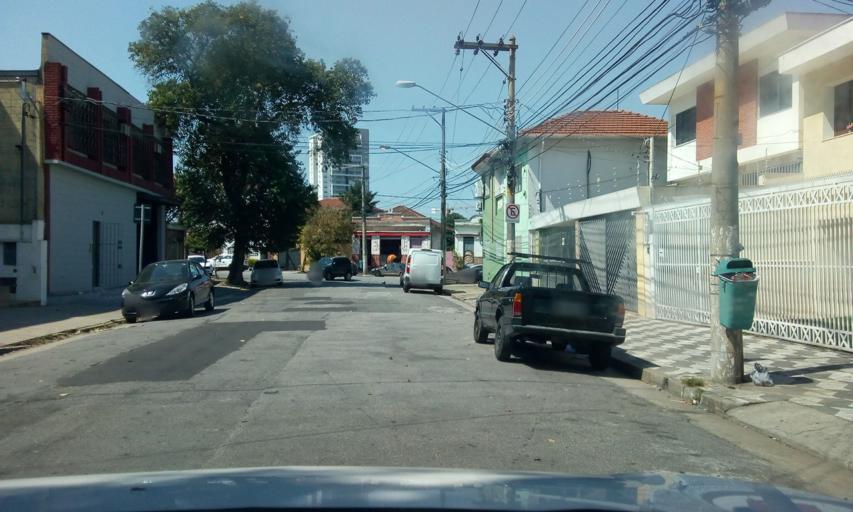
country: BR
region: Sao Paulo
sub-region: Osasco
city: Osasco
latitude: -23.5152
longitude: -46.7181
